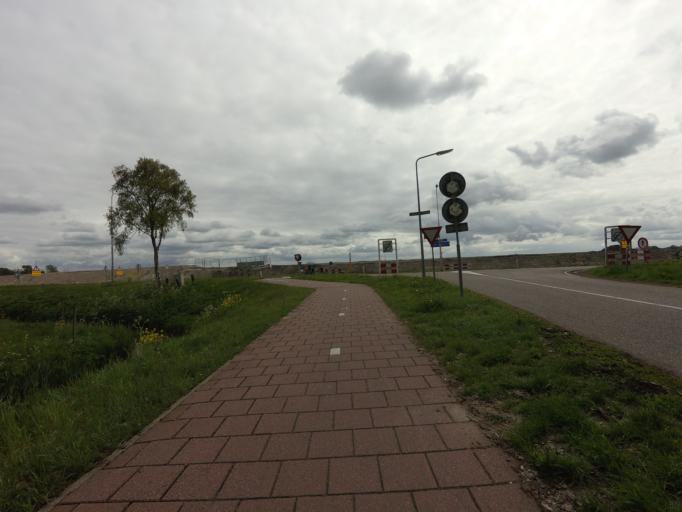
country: NL
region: North Holland
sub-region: Gemeente Weesp
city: Weesp
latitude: 52.2916
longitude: 5.0836
